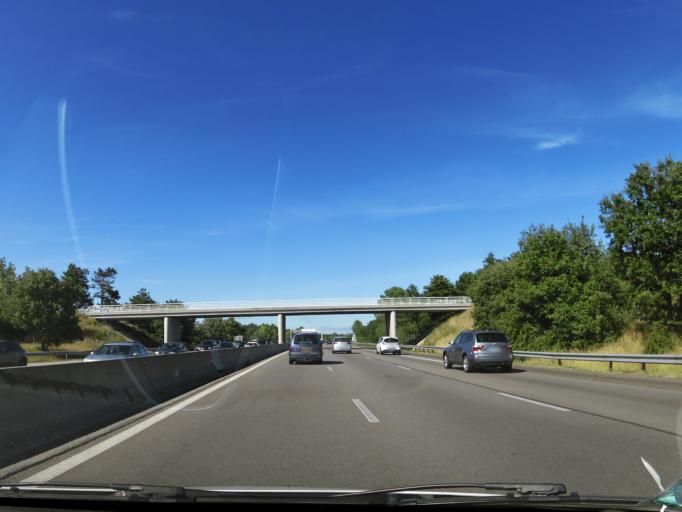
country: FR
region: Rhone-Alpes
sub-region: Departement de la Drome
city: Allan
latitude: 44.5051
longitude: 4.7708
